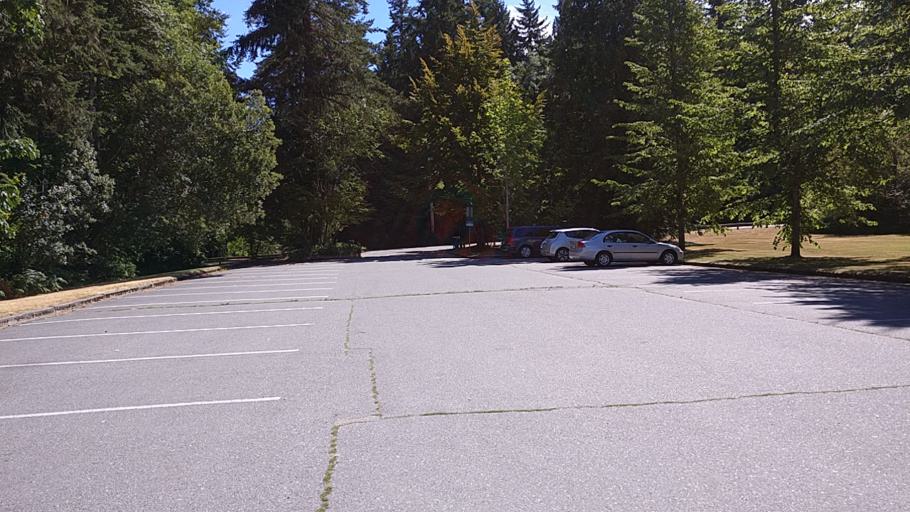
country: CA
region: British Columbia
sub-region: Greater Vancouver Regional District
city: White Rock
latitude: 49.0504
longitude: -122.8573
